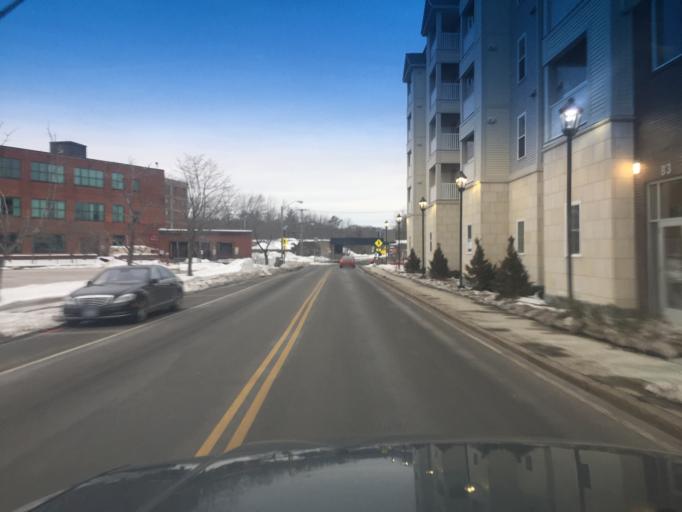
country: US
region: Massachusetts
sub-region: Norfolk County
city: Walpole
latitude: 42.1457
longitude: -71.2549
